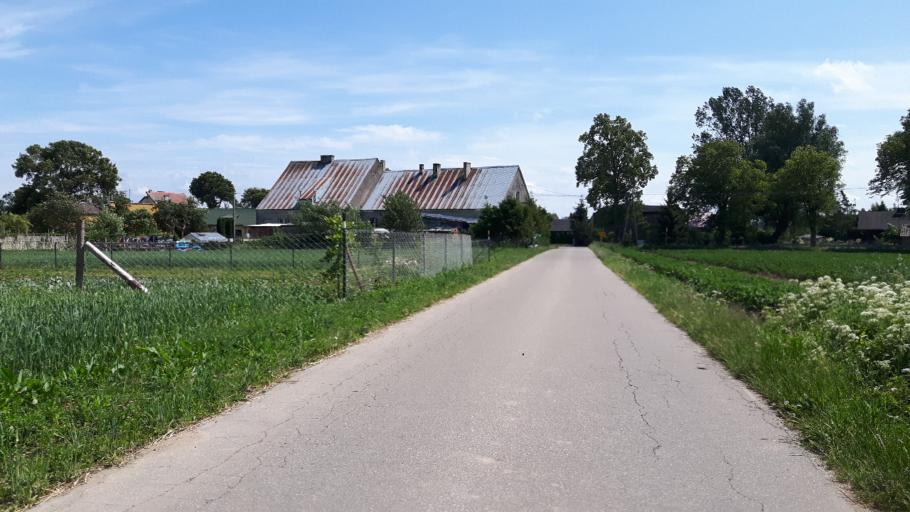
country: PL
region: Pomeranian Voivodeship
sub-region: Powiat wejherowski
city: Gniewino
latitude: 54.7241
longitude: 17.9606
